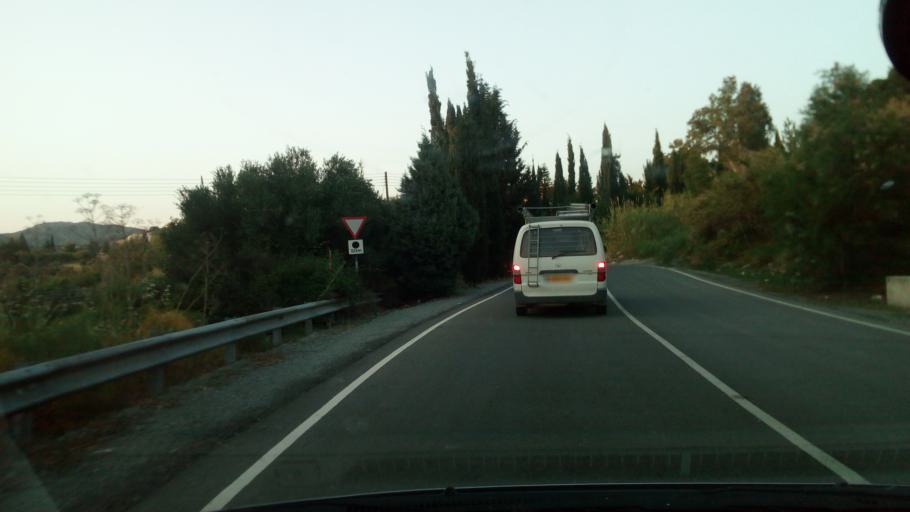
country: CY
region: Larnaka
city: Kofinou
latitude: 34.8212
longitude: 33.3759
